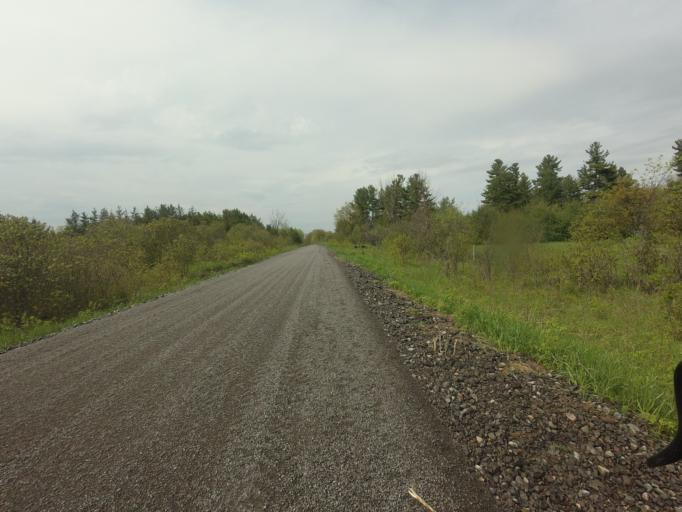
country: CA
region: Ontario
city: Carleton Place
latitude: 45.1578
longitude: -76.1450
